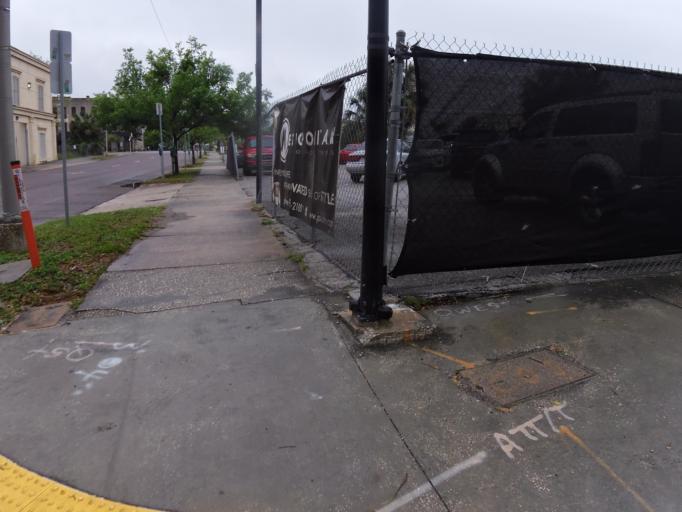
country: US
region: Florida
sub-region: Duval County
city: Jacksonville
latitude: 30.3314
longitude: -81.6631
